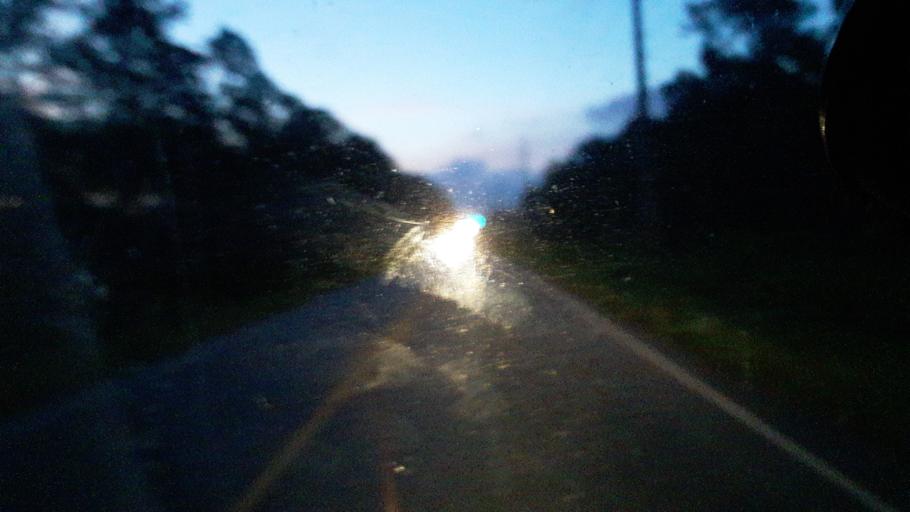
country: US
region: North Carolina
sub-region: Brunswick County
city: Oak Island
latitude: 33.9984
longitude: -78.2411
